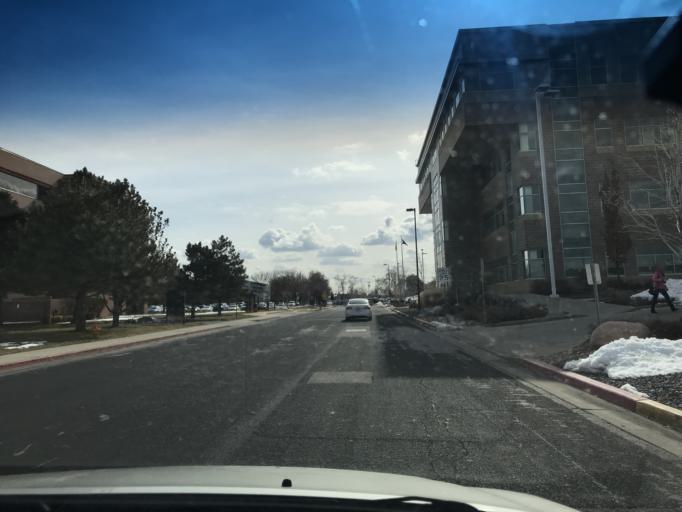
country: US
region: Utah
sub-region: Salt Lake County
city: Salt Lake City
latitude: 40.7753
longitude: -111.9475
